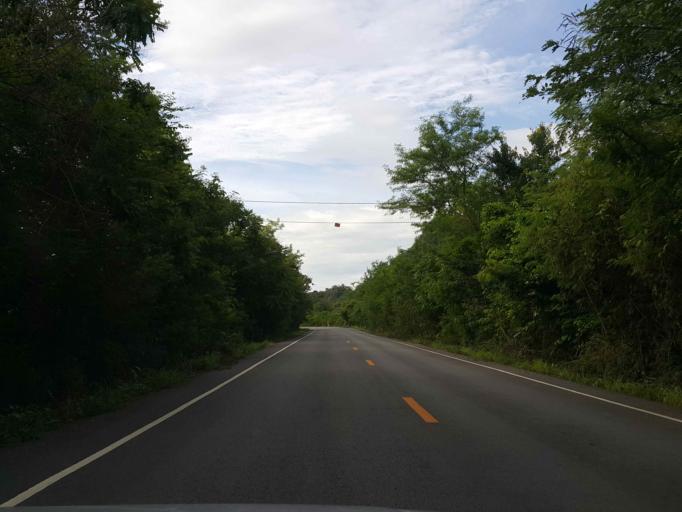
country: TH
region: Sukhothai
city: Thung Saliam
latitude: 17.2838
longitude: 99.5272
